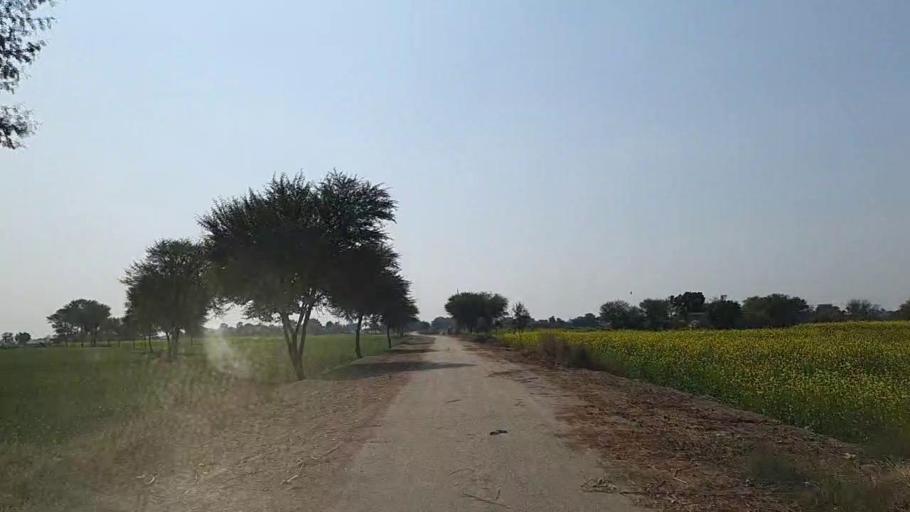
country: PK
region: Sindh
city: Nawabshah
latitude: 26.2515
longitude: 68.4867
